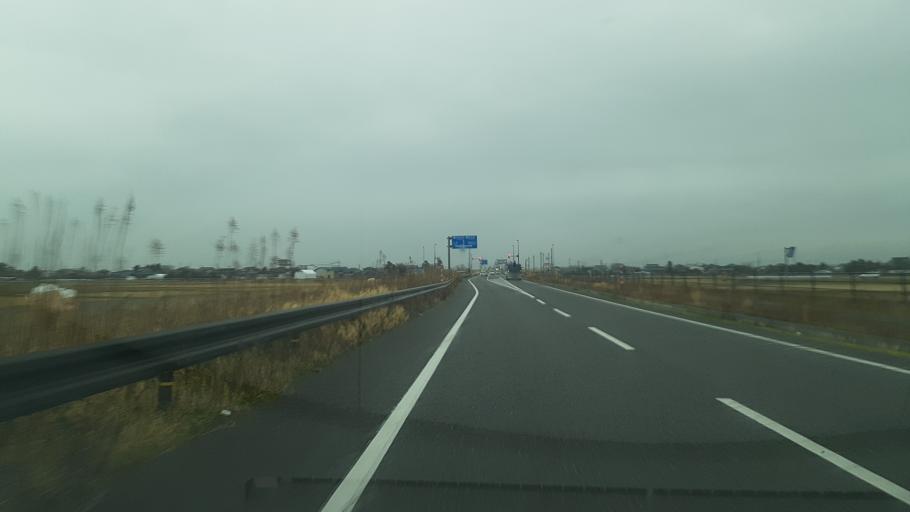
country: JP
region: Niigata
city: Kameda-honcho
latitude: 37.8731
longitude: 139.1534
